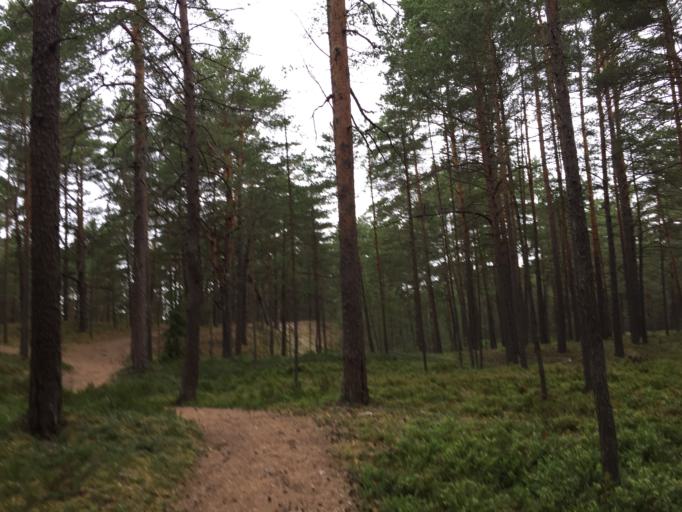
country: LV
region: Carnikava
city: Carnikava
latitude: 57.1212
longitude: 24.2194
